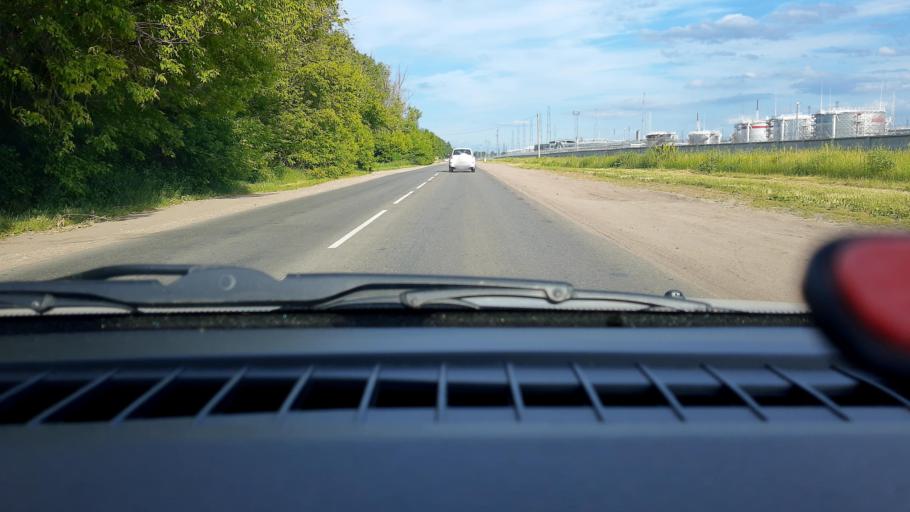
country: RU
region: Nizjnij Novgorod
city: Kstovo
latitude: 56.1240
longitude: 44.1282
